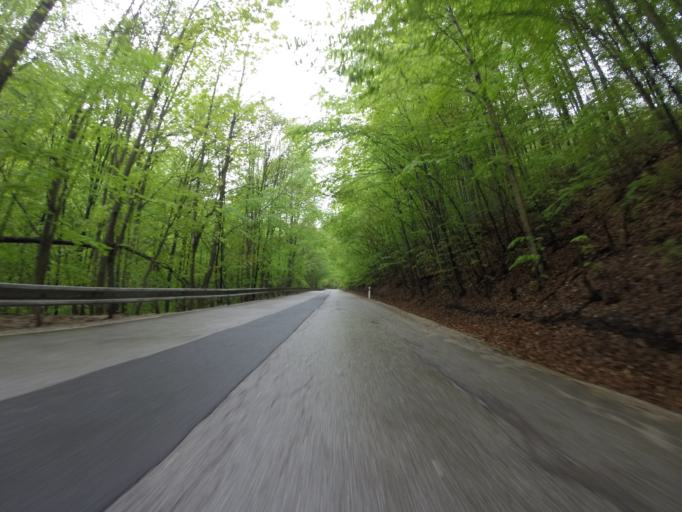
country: SK
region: Banskobystricky
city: Revuca
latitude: 48.7606
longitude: 20.0893
